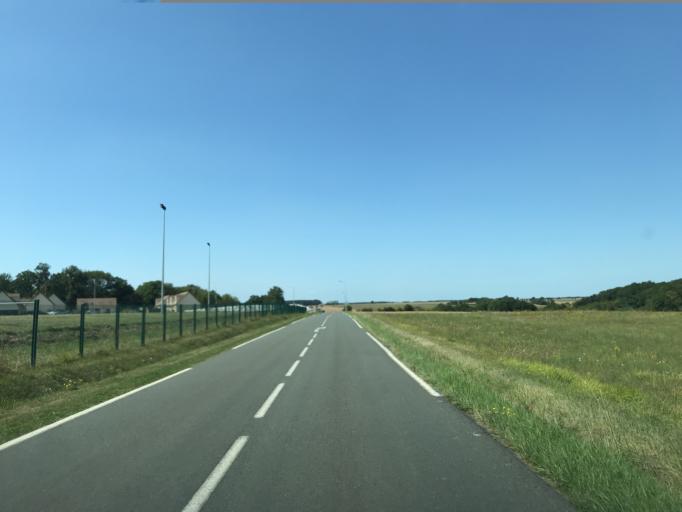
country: FR
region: Haute-Normandie
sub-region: Departement de l'Eure
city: La Chapelle-Reanville
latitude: 49.0968
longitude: 1.3860
